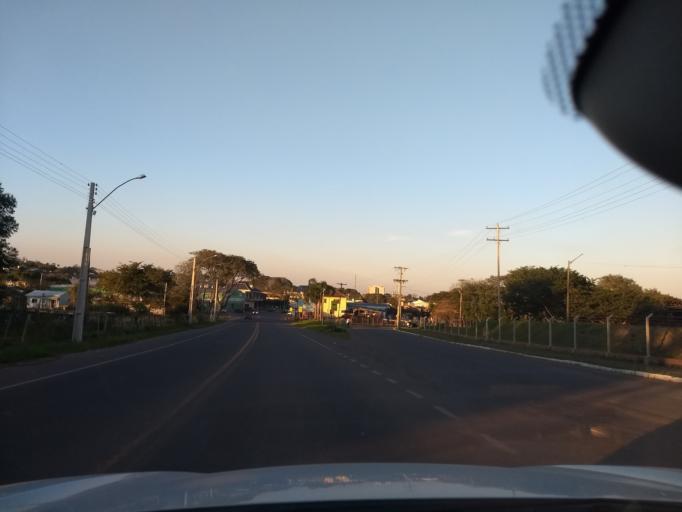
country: BR
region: Rio Grande do Sul
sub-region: Santa Cruz Do Sul
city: Santa Cruz do Sul
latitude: -29.7206
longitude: -52.5176
